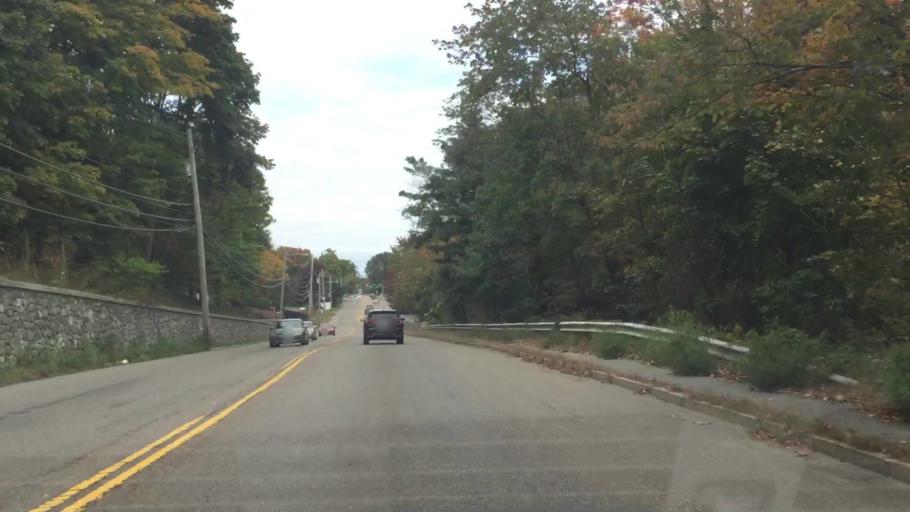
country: US
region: Massachusetts
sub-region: Essex County
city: Middleton
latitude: 42.5970
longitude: -71.0180
